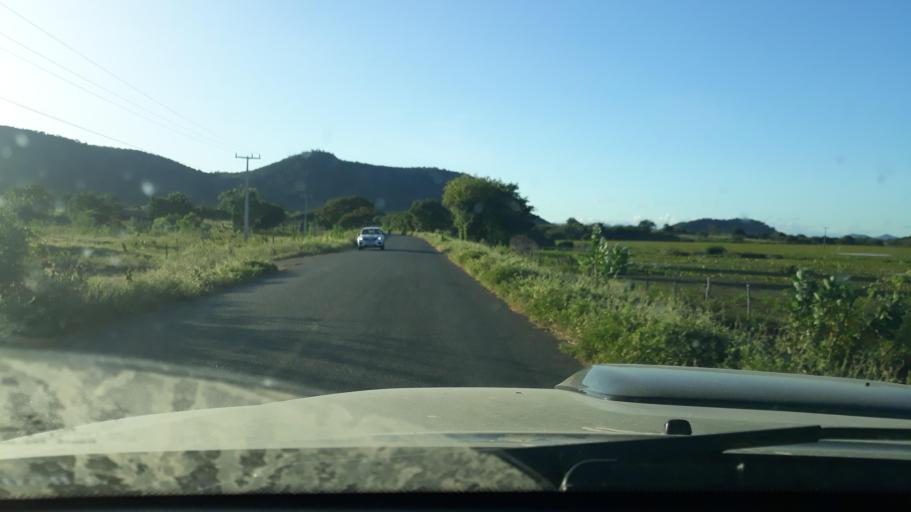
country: BR
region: Bahia
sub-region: Guanambi
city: Guanambi
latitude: -14.1171
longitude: -42.8593
